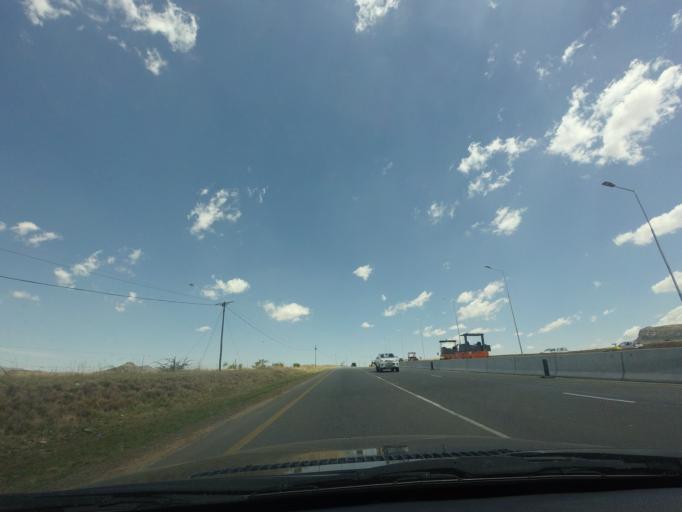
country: LS
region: Maseru
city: Maseru
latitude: -29.2936
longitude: 27.4405
